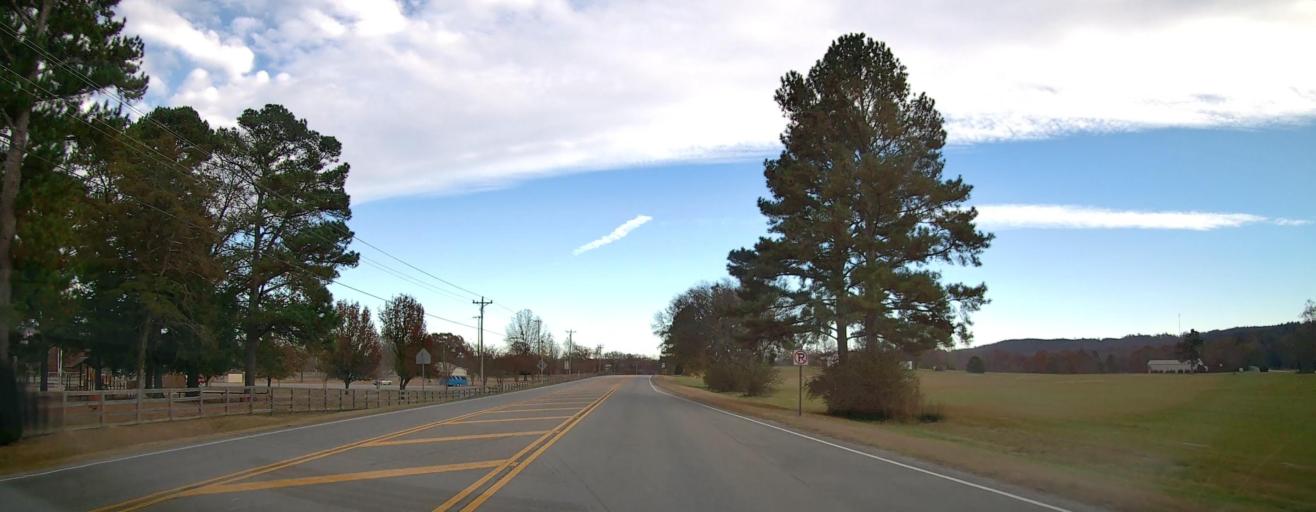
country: US
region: Alabama
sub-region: Morgan County
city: Falkville
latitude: 34.4154
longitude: -86.7037
